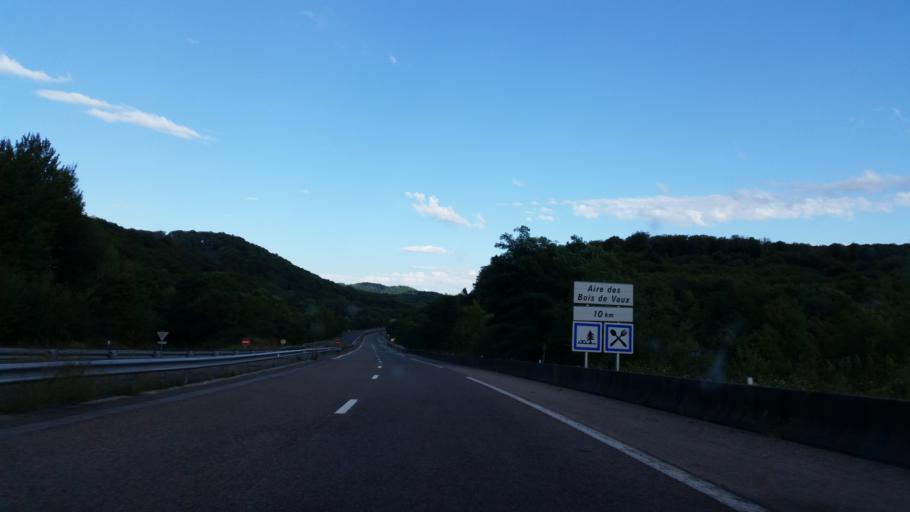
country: FR
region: Franche-Comte
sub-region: Departement de la Haute-Saone
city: Ronchamp
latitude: 47.6366
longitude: 6.6182
